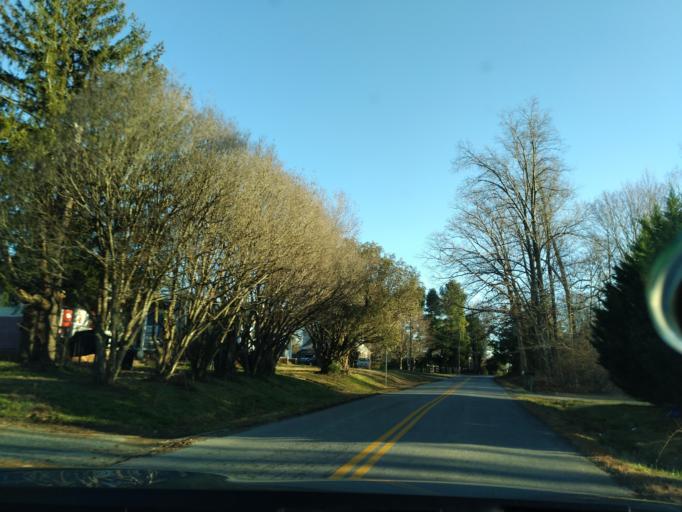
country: US
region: Virginia
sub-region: Prince Edward County
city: Hampden Sydney
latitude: 37.3069
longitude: -78.5611
